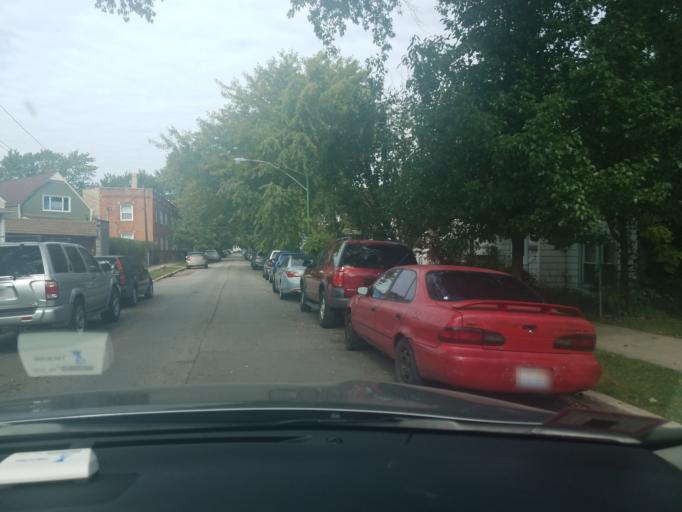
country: US
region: Illinois
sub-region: Cook County
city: Lincolnwood
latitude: 41.9622
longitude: -87.7333
